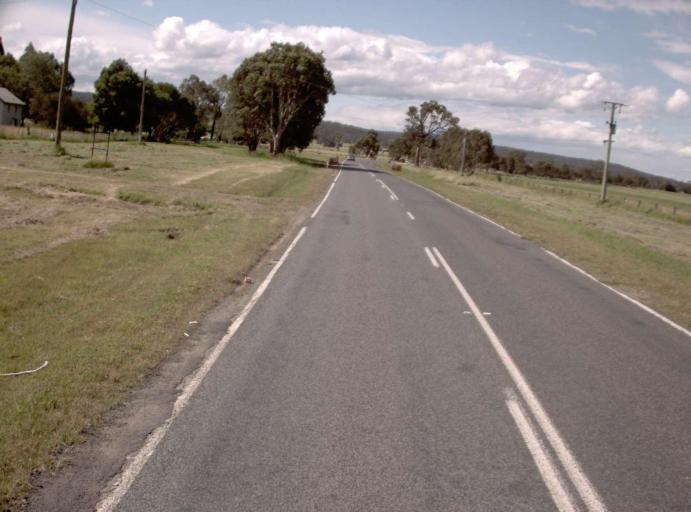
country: AU
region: Victoria
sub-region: Latrobe
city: Traralgon
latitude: -38.1498
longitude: 146.5230
